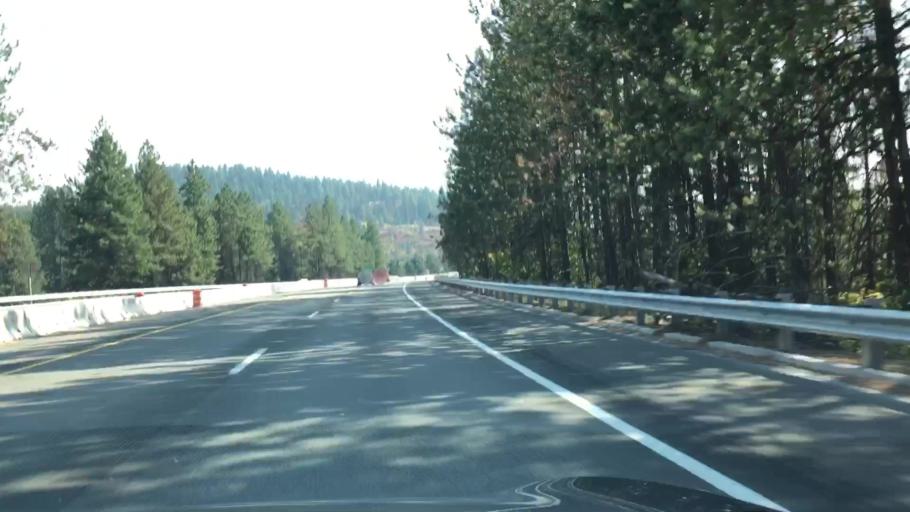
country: US
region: Idaho
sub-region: Kootenai County
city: Coeur d'Alene
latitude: 47.6749
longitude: -116.7519
